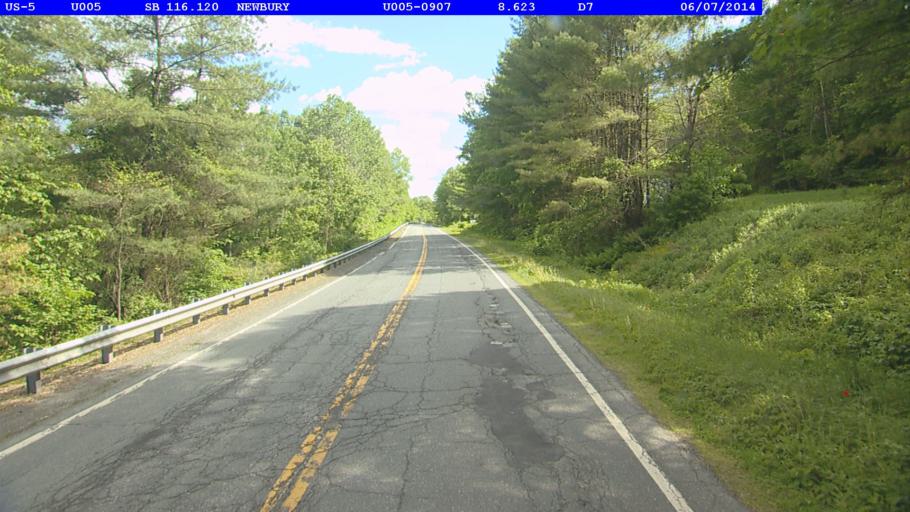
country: US
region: New Hampshire
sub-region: Grafton County
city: Woodsville
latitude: 44.1422
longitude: -72.0427
